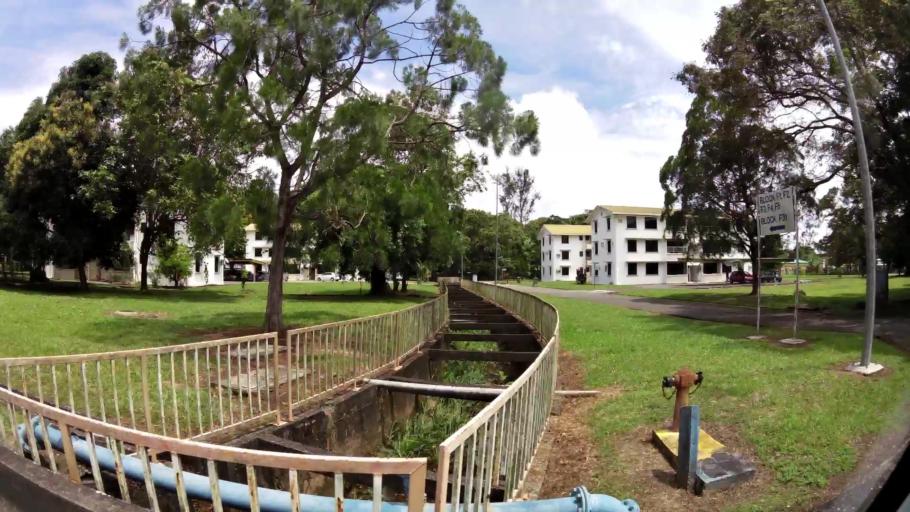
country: BN
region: Brunei and Muara
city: Bandar Seri Begawan
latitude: 4.9184
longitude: 114.9320
